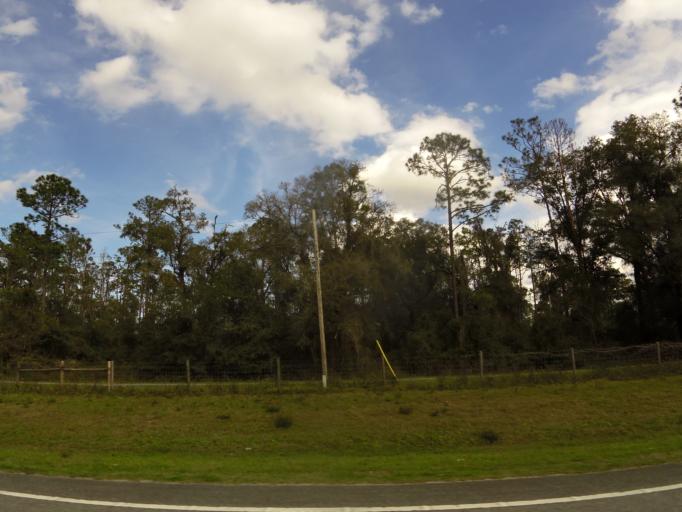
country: US
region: Florida
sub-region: Volusia County
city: De Leon Springs
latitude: 29.2280
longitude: -81.3232
